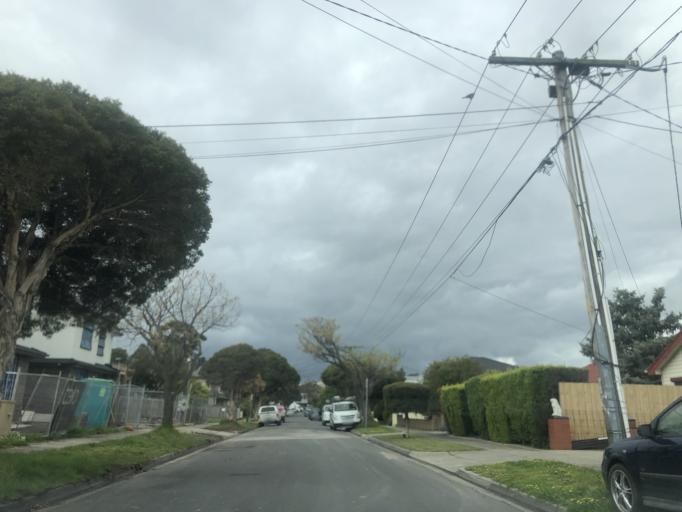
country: AU
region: Victoria
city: Clayton
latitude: -37.9200
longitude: 145.1166
